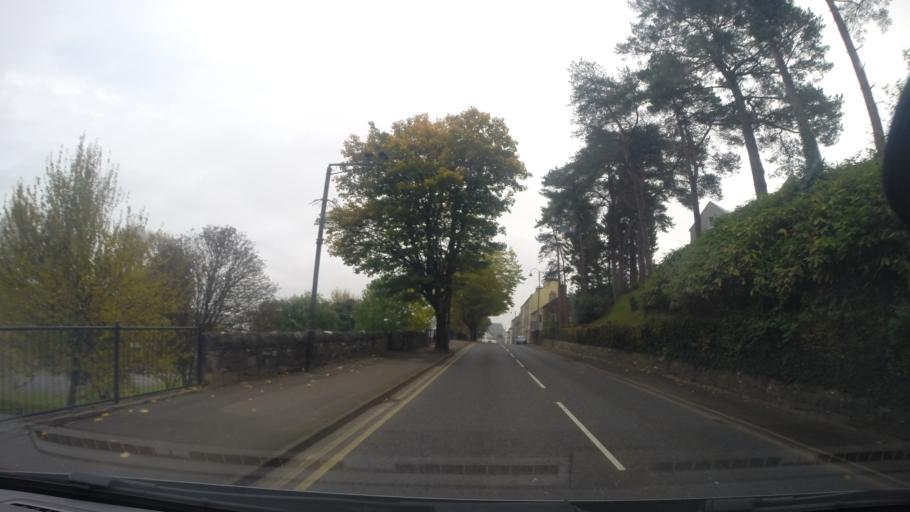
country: GB
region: Northern Ireland
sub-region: Fermanagh District
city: Enniskillen
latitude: 54.3484
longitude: -7.6494
